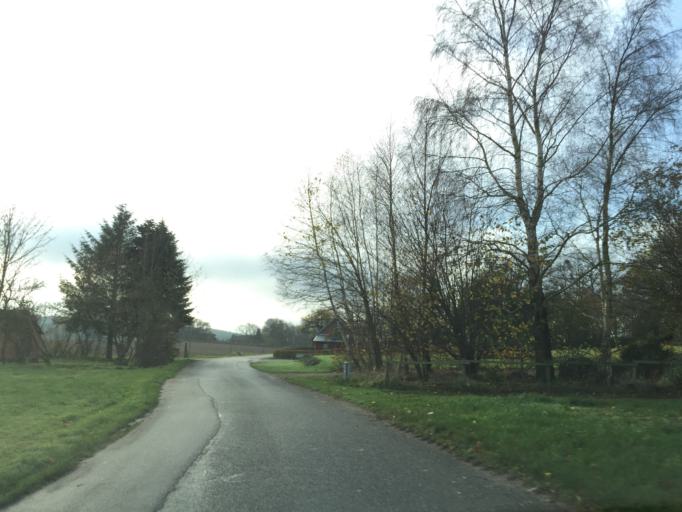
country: DK
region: Central Jutland
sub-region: Skanderborg Kommune
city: Ry
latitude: 56.1692
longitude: 9.7879
